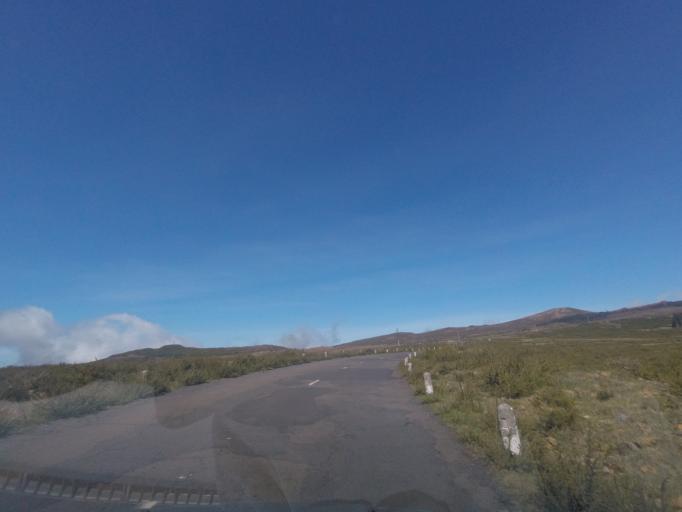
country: PT
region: Madeira
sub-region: Calheta
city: Arco da Calheta
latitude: 32.7530
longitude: -17.0989
